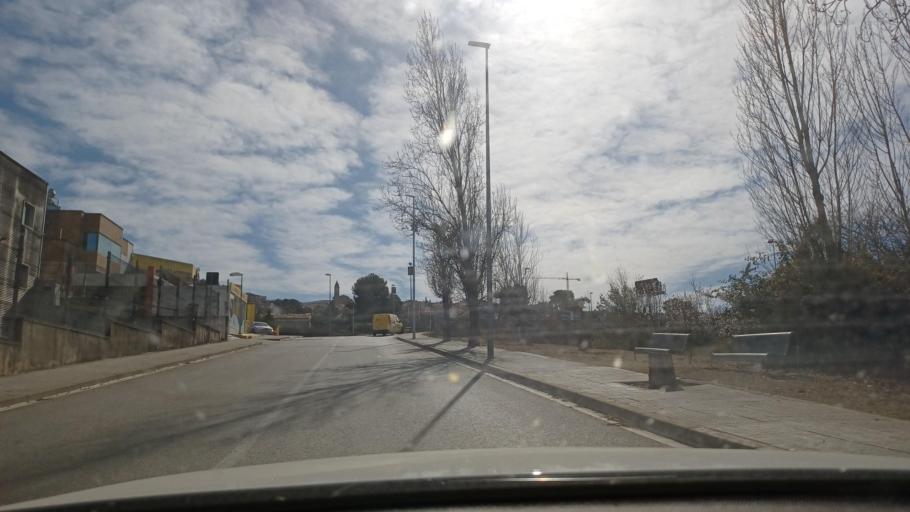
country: ES
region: Catalonia
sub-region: Provincia de Barcelona
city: Gelida
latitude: 41.4472
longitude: 1.8650
